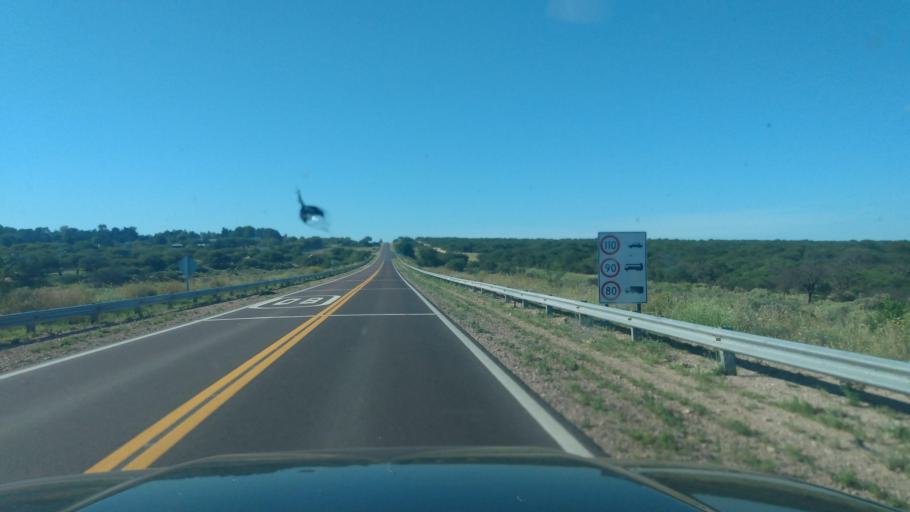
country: AR
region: La Pampa
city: Santa Rosa
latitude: -36.7189
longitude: -64.2831
